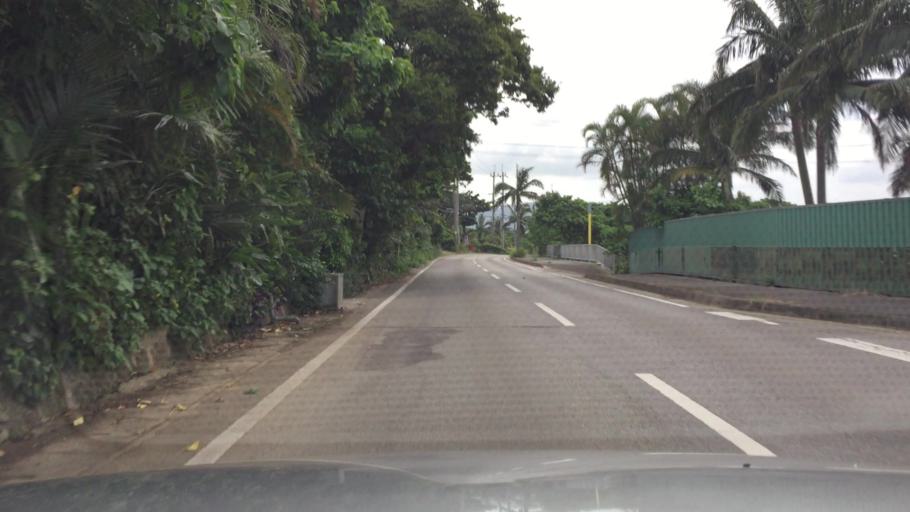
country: JP
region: Okinawa
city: Ishigaki
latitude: 24.4539
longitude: 124.1943
